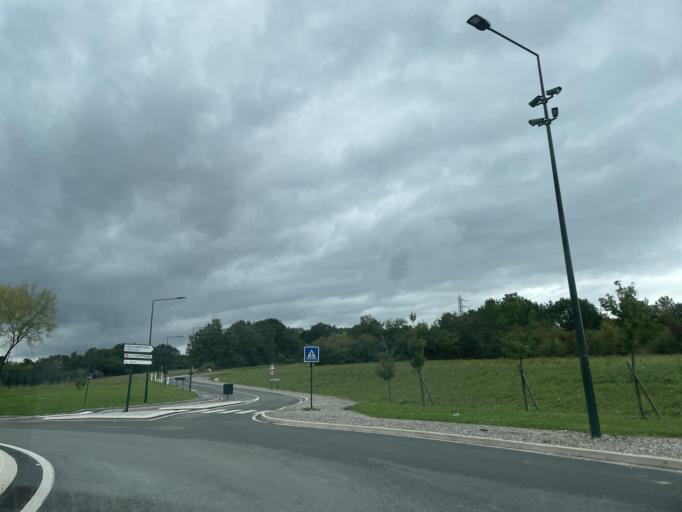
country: FR
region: Ile-de-France
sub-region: Departement de Seine-et-Marne
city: Coulommiers
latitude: 48.8154
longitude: 3.1077
